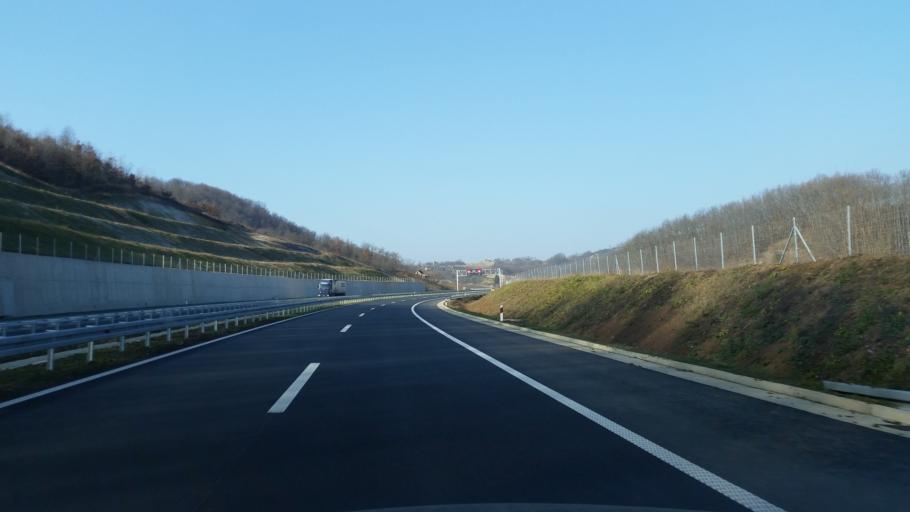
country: RS
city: Prislonica
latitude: 44.0075
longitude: 20.3884
